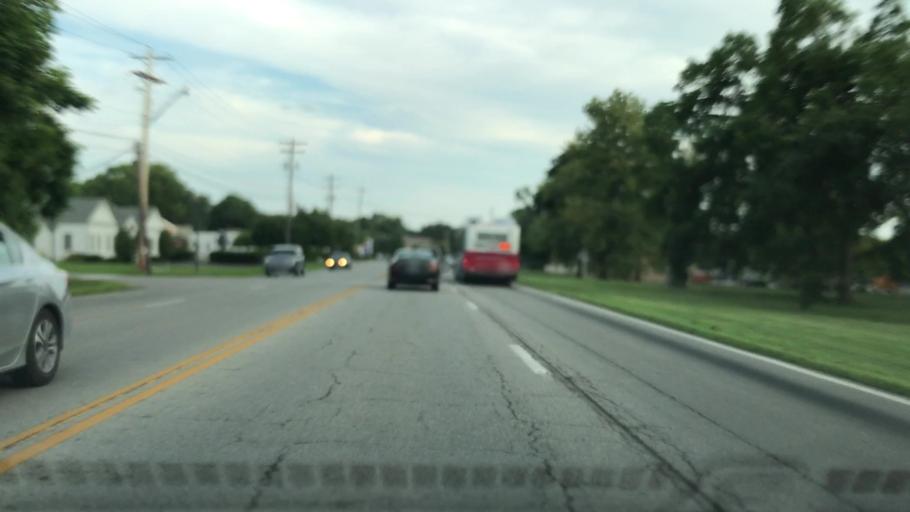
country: US
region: Ohio
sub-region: Franklin County
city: Upper Arlington
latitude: 40.0186
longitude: -83.0917
